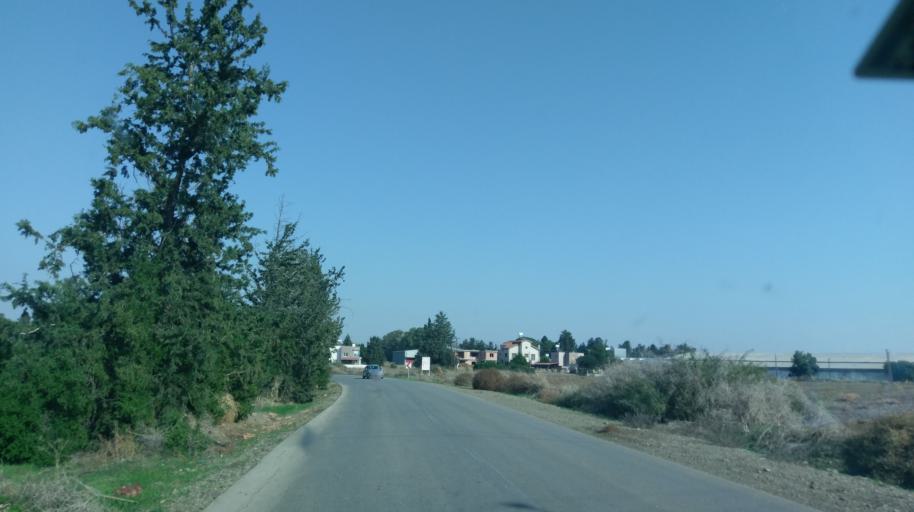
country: CY
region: Lefkosia
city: Morfou
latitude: 35.1880
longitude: 32.9671
